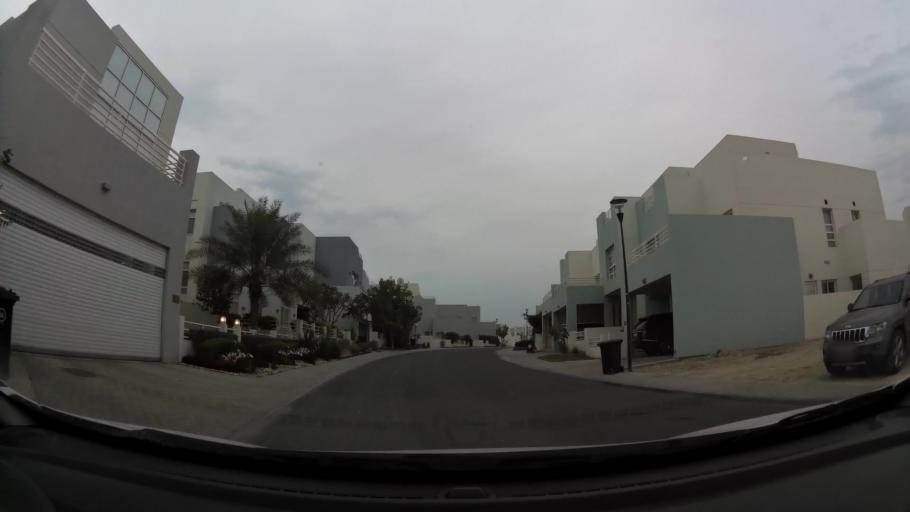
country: BH
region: Northern
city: Ar Rifa'
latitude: 26.0933
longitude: 50.5636
